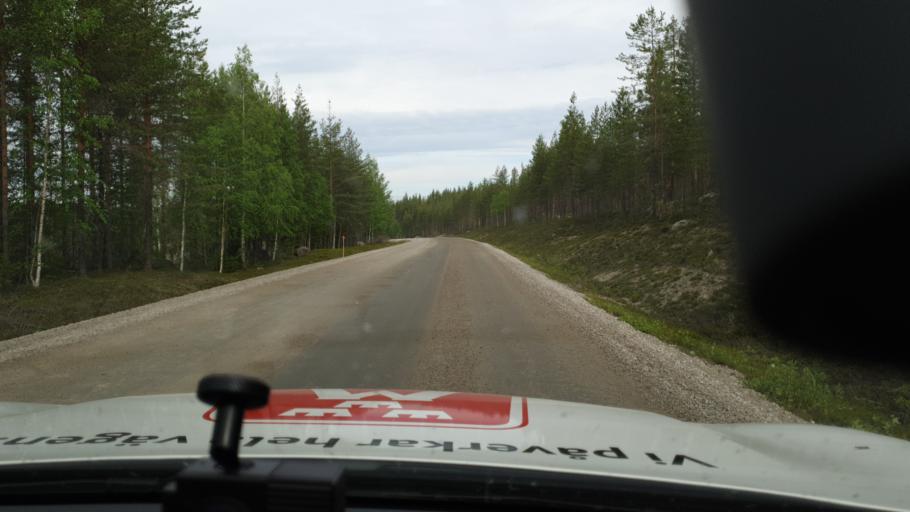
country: SE
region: Vaesterbotten
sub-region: Lycksele Kommun
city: Lycksele
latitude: 64.8545
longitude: 18.7439
